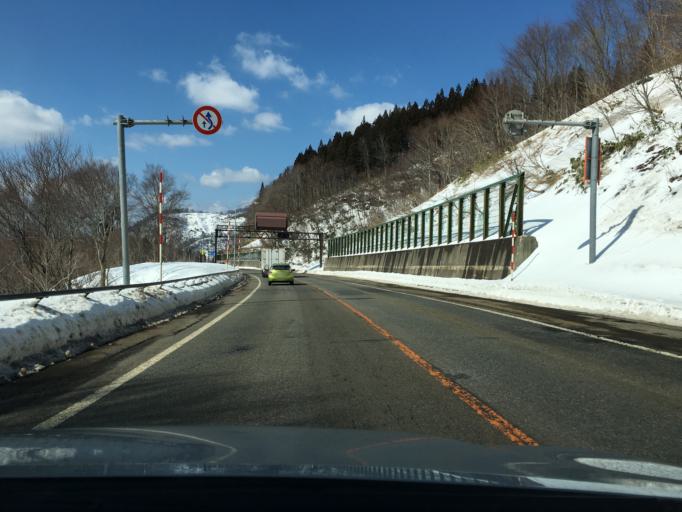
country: JP
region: Yamagata
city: Tsuruoka
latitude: 38.5655
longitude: 139.9394
